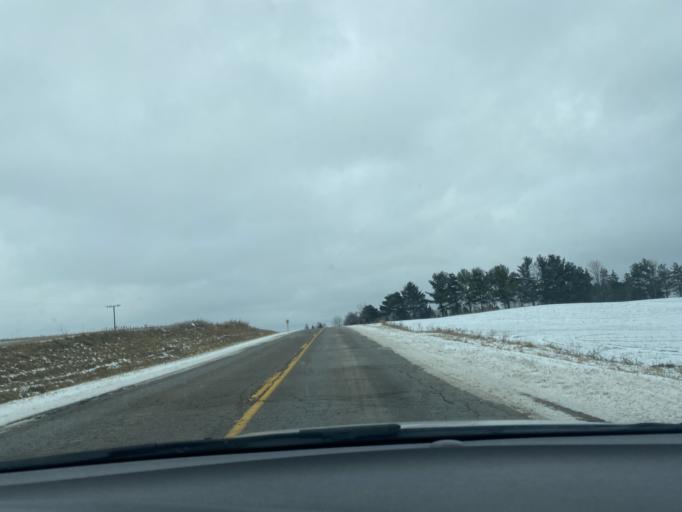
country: US
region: Michigan
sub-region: Lapeer County
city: North Branch
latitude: 43.2091
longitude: -83.1356
